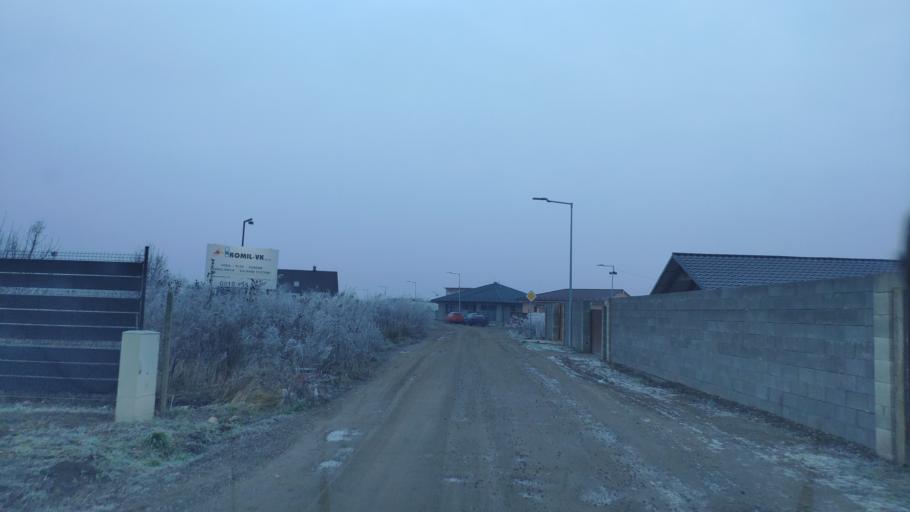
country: SK
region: Kosicky
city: Kosice
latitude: 48.6162
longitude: 21.3271
